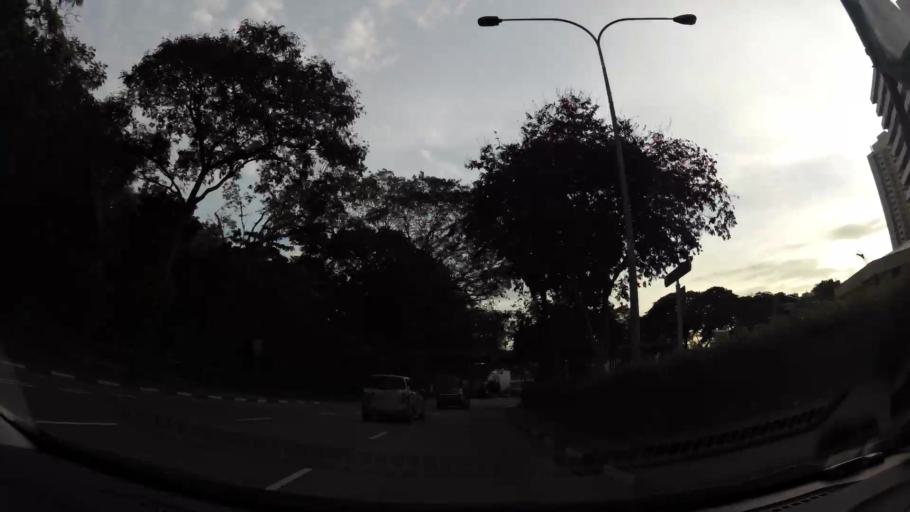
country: SG
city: Singapore
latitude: 1.2872
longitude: 103.8351
